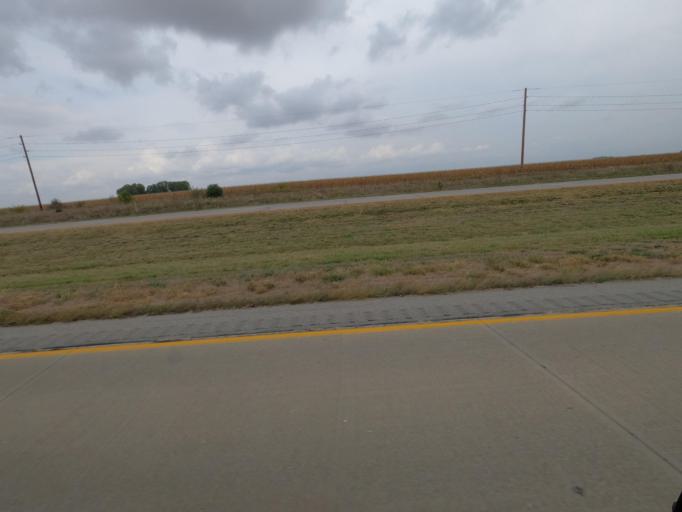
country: US
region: Iowa
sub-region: Jasper County
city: Monroe
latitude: 41.5617
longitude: -93.1528
